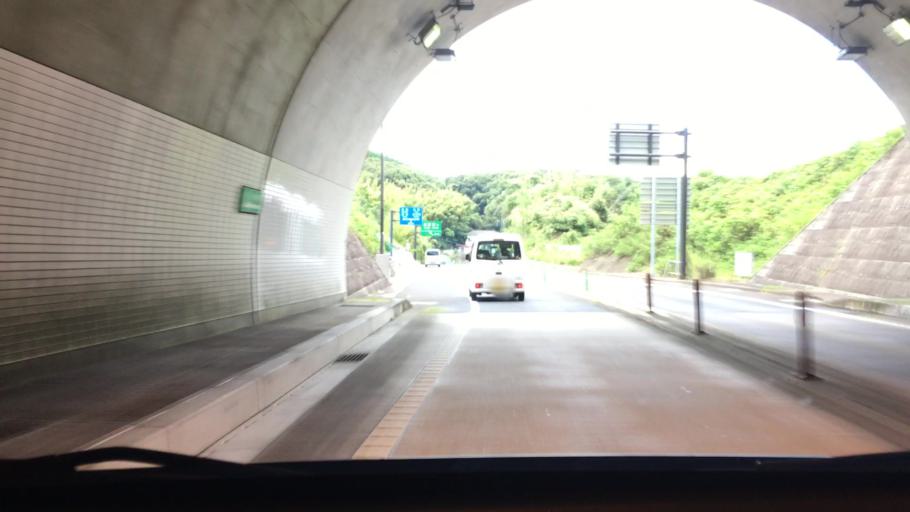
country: JP
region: Nagasaki
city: Sasebo
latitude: 33.1018
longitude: 129.7796
